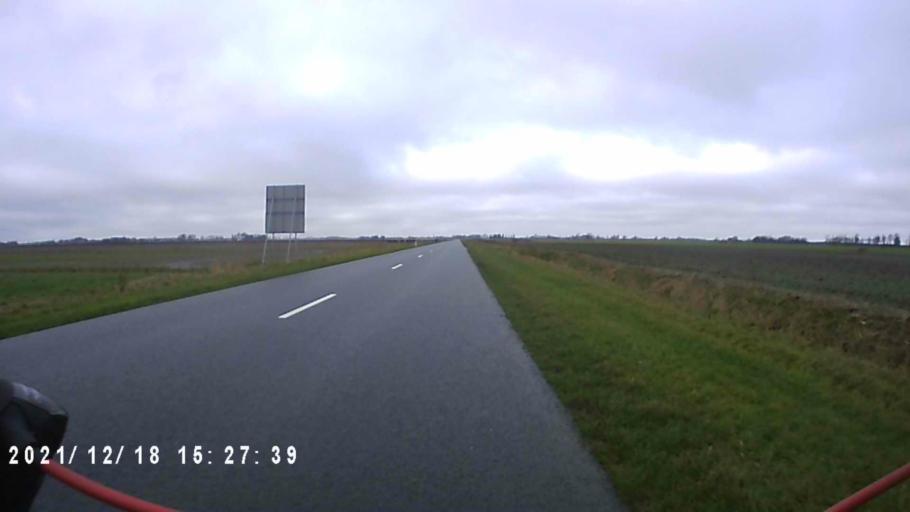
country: NL
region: Friesland
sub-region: Gemeente Dongeradeel
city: Anjum
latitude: 53.3300
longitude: 6.1465
